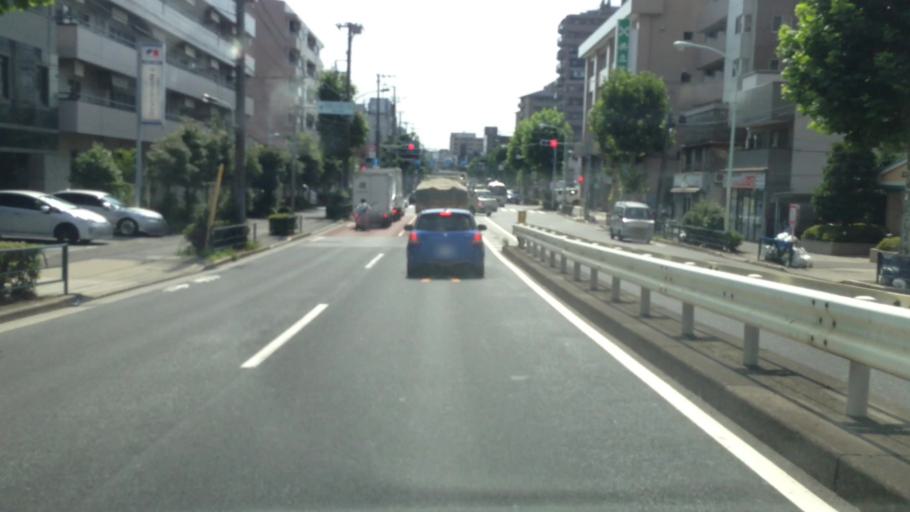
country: JP
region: Kanagawa
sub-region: Kawasaki-shi
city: Kawasaki
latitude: 35.5800
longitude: 139.7255
